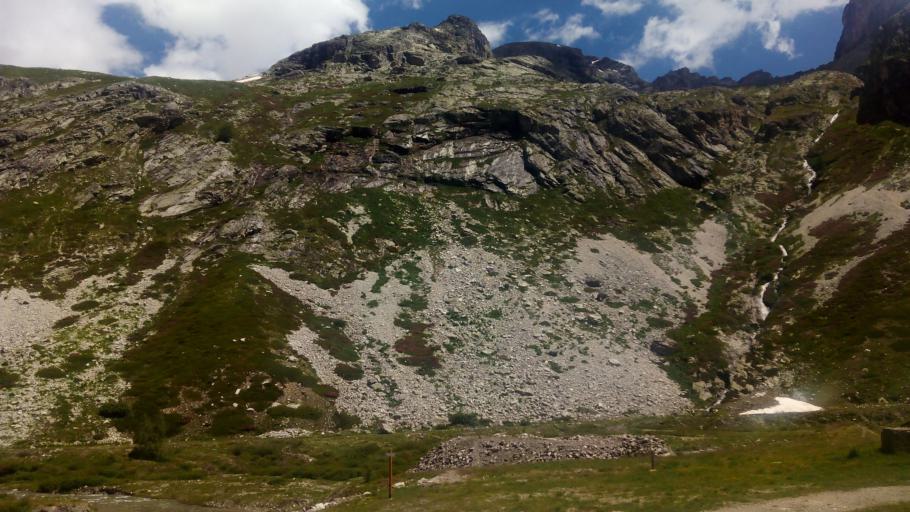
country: IT
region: Piedmont
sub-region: Provincia di Torino
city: Oulx
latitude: 45.1322
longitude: 6.8026
